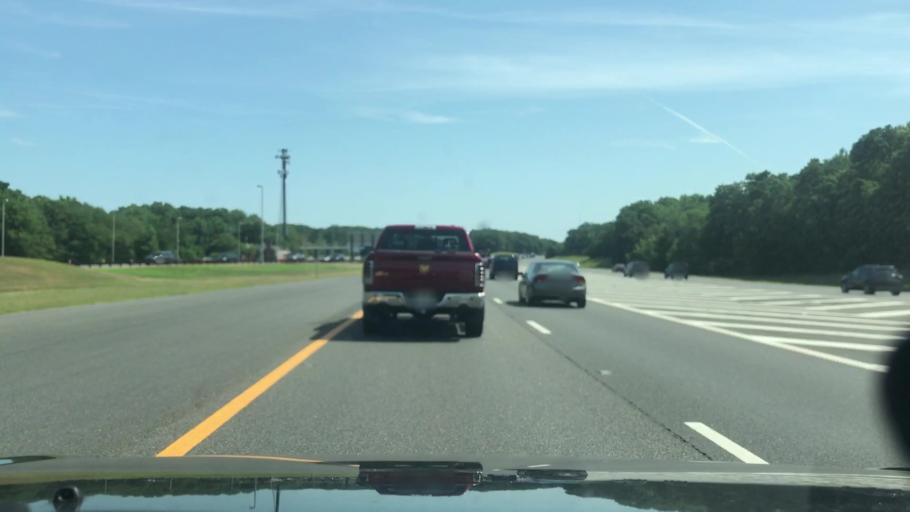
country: US
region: New Jersey
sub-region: Monmouth County
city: Eatontown
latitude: 40.2537
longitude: -74.0815
